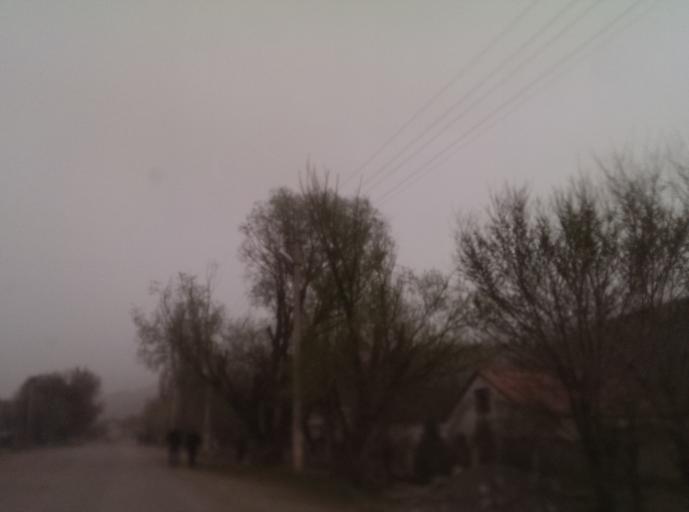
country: KG
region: Naryn
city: Naryn
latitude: 41.4234
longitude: 76.0155
